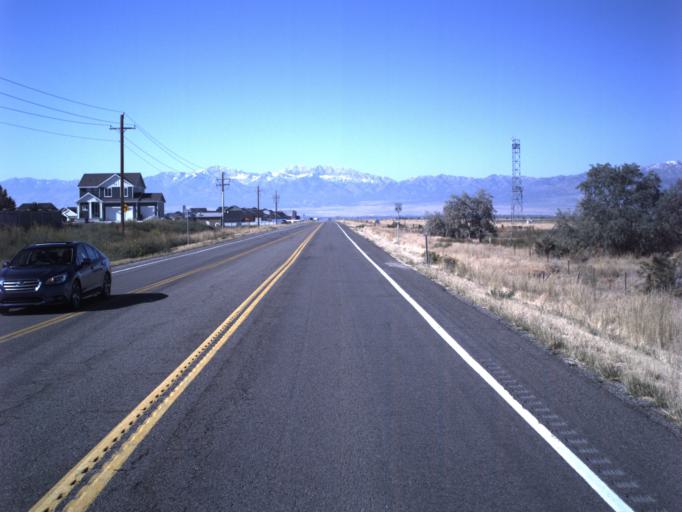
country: US
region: Utah
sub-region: Tooele County
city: Stansbury park
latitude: 40.6423
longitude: -112.3146
